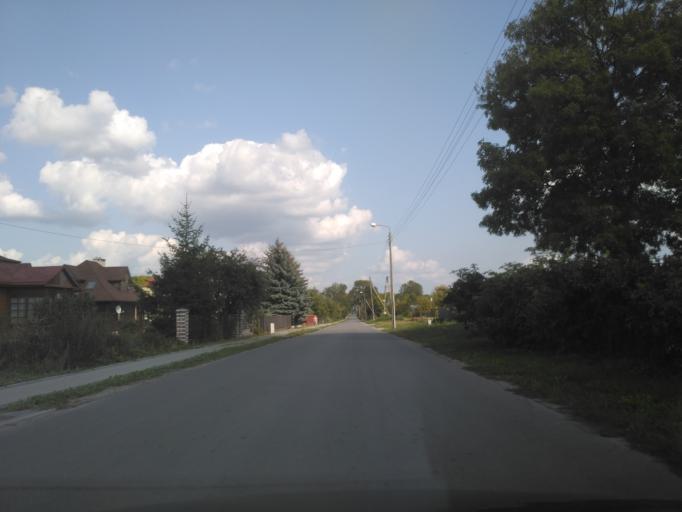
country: PL
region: Lublin Voivodeship
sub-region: Powiat chelmski
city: Pokrowka
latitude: 51.0689
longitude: 23.5060
